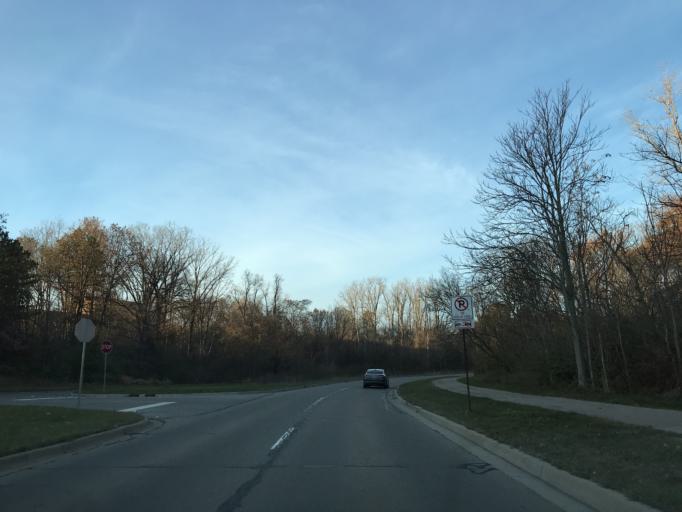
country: US
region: Michigan
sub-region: Washtenaw County
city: Ann Arbor
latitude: 42.2914
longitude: -83.7048
